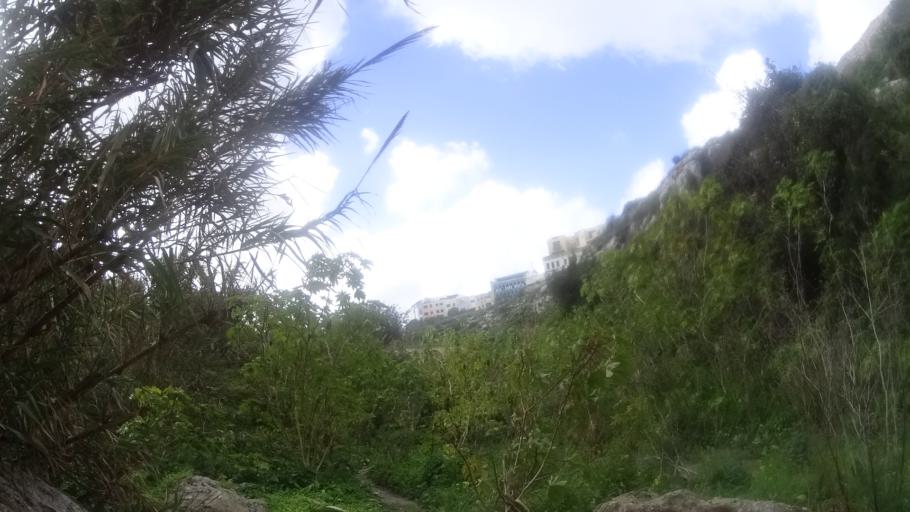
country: MT
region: Il-Mosta
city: Mosta
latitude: 35.9174
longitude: 14.4268
